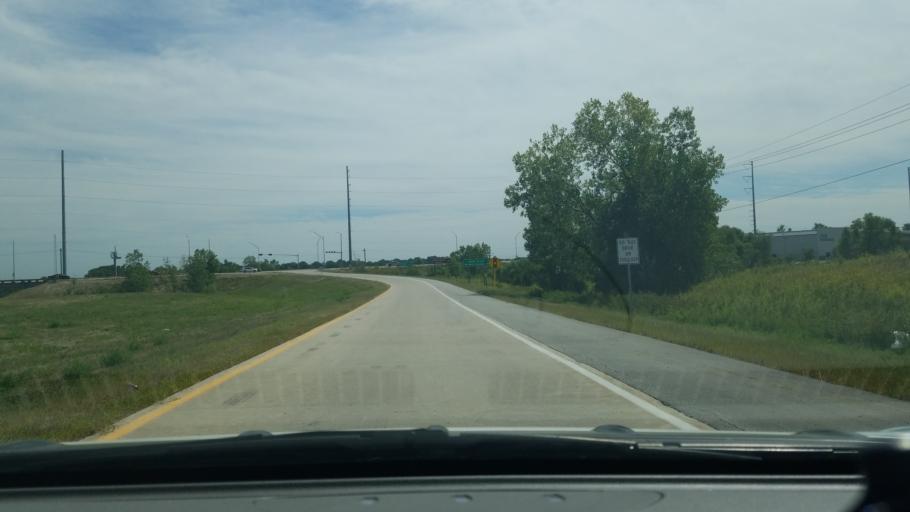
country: US
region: Nebraska
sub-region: Sarpy County
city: Chalco
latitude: 41.1469
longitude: -96.1419
